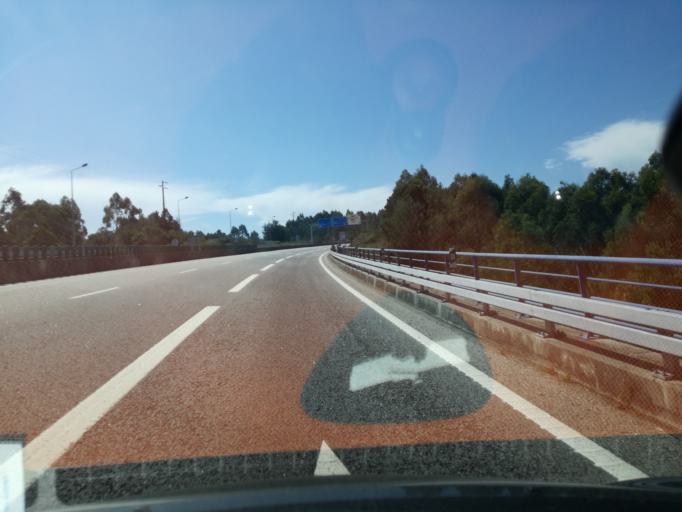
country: PT
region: Viana do Castelo
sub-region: Caminha
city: Vila Praia de Ancora
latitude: 41.8517
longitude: -8.7745
